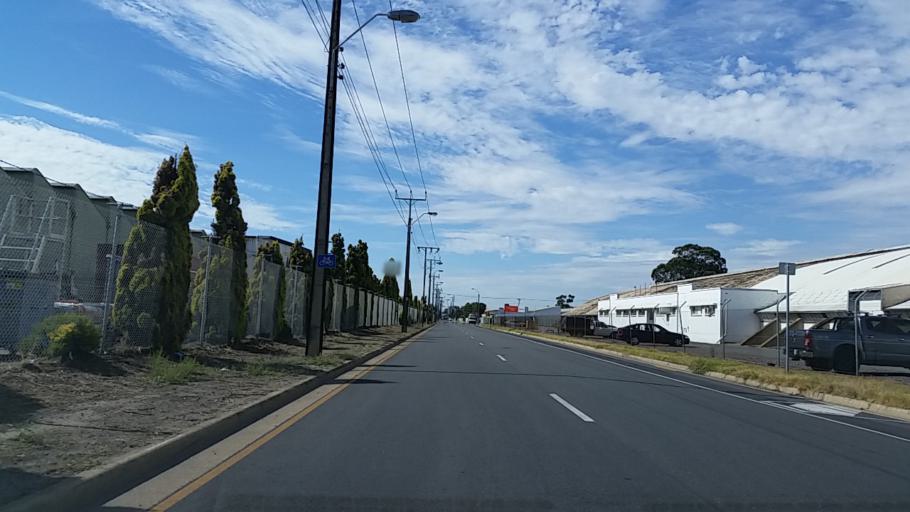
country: AU
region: South Australia
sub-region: Charles Sturt
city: Woodville North
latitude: -34.8582
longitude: 138.5384
